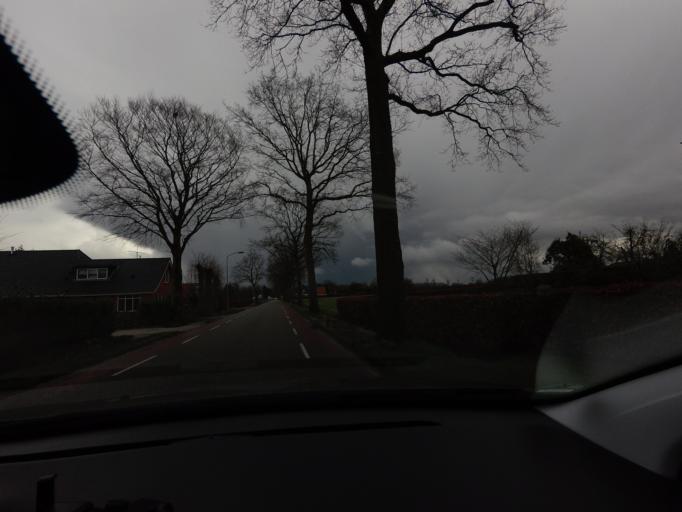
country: NL
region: Drenthe
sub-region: Gemeente Borger-Odoorn
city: Borger
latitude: 52.9922
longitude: 6.7744
